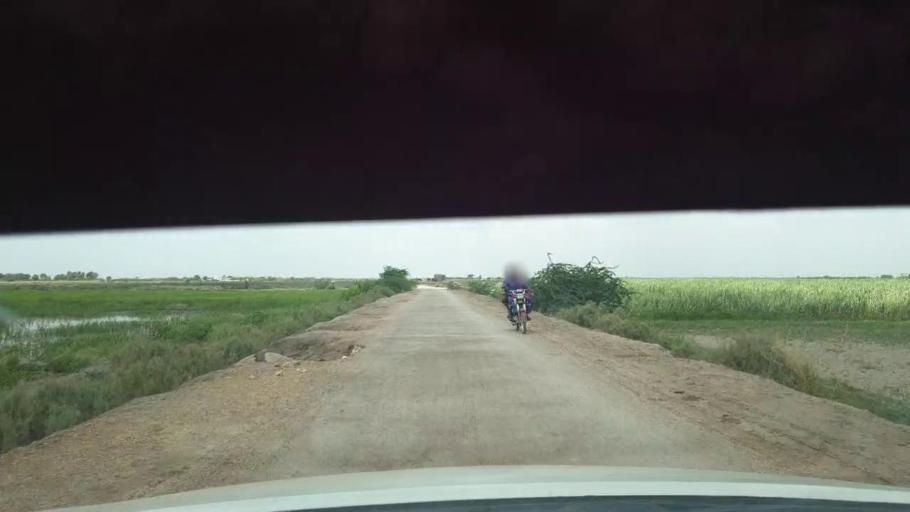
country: PK
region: Sindh
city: Kadhan
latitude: 24.5450
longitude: 69.1252
